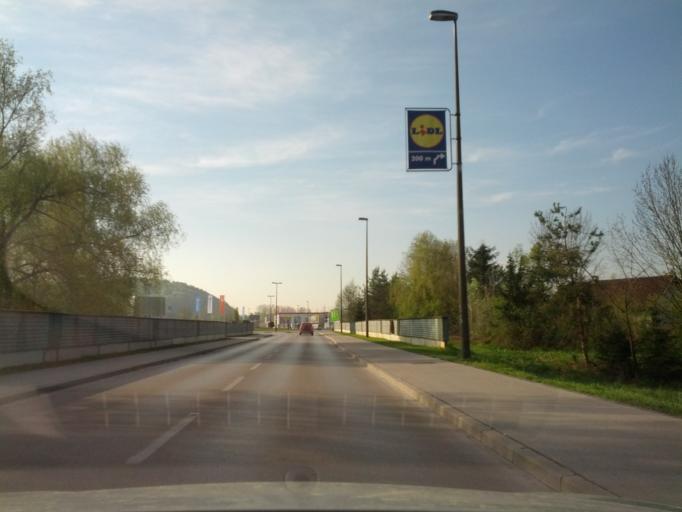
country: SI
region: Skofljica
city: Lavrica
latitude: 46.0226
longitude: 14.5333
